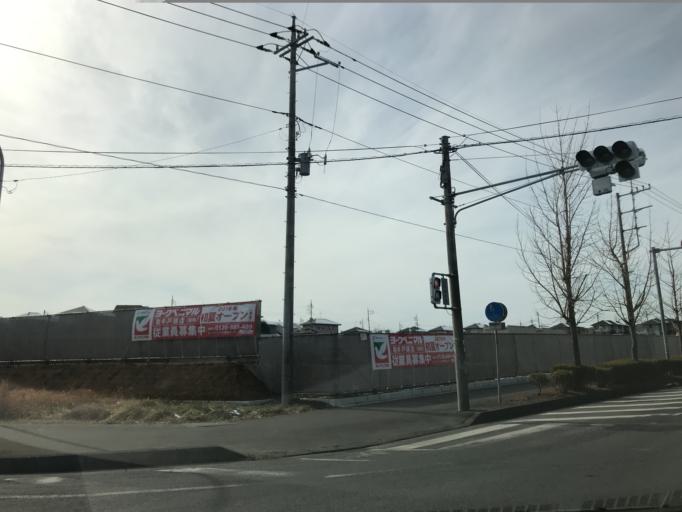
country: JP
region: Ibaraki
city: Moriya
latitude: 35.9227
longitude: 140.0043
